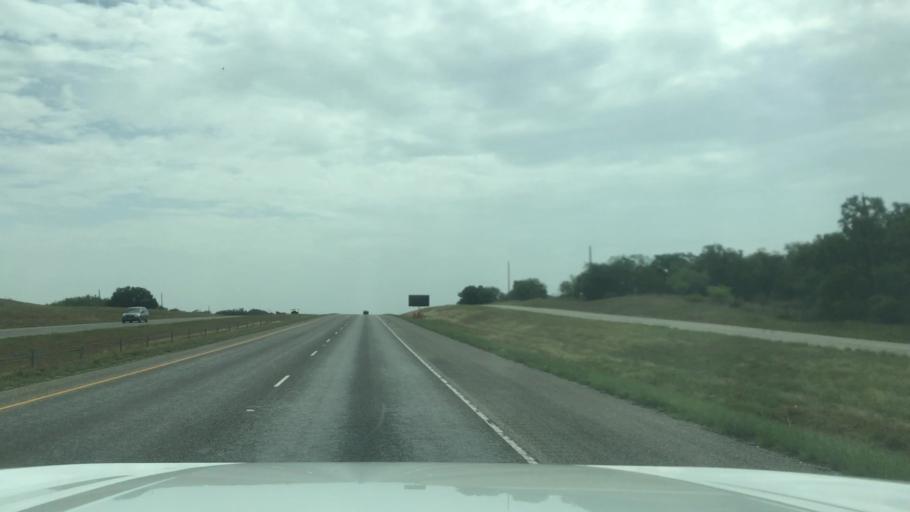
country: US
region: Texas
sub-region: Eastland County
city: Cisco
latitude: 32.3753
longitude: -99.0303
